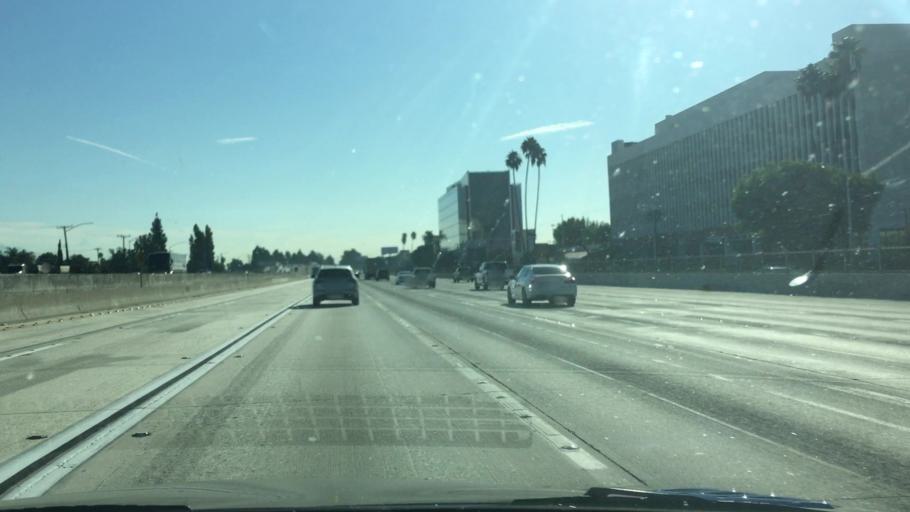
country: US
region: California
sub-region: Los Angeles County
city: Rosemead
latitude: 34.0723
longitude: -118.0624
